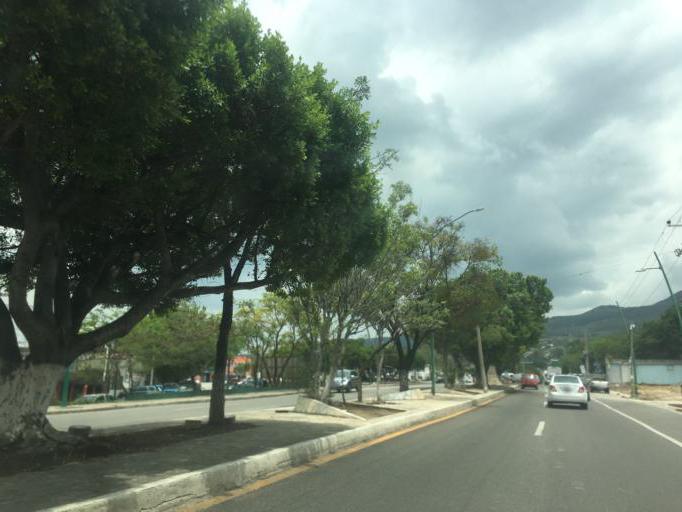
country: MX
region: Chiapas
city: Tuxtla Gutierrez
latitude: 16.7520
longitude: -93.1418
